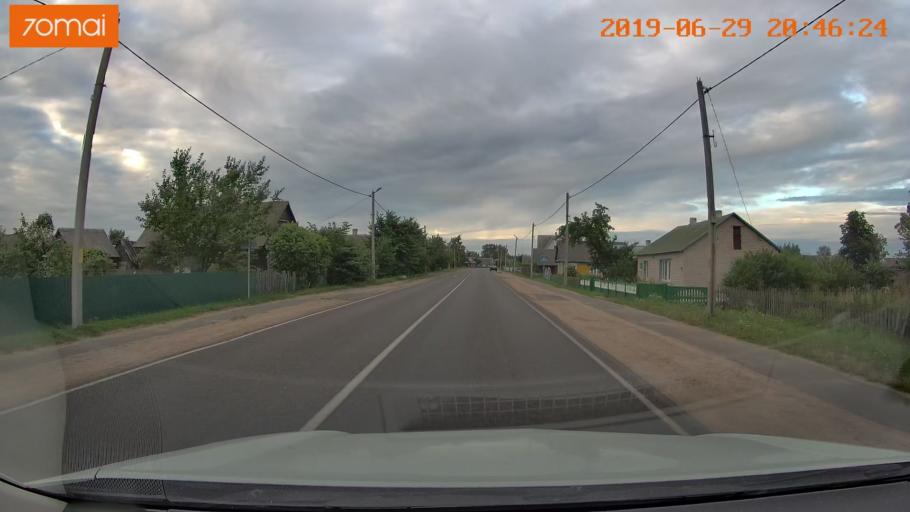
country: BY
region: Brest
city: Hantsavichy
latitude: 52.6306
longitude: 26.3083
